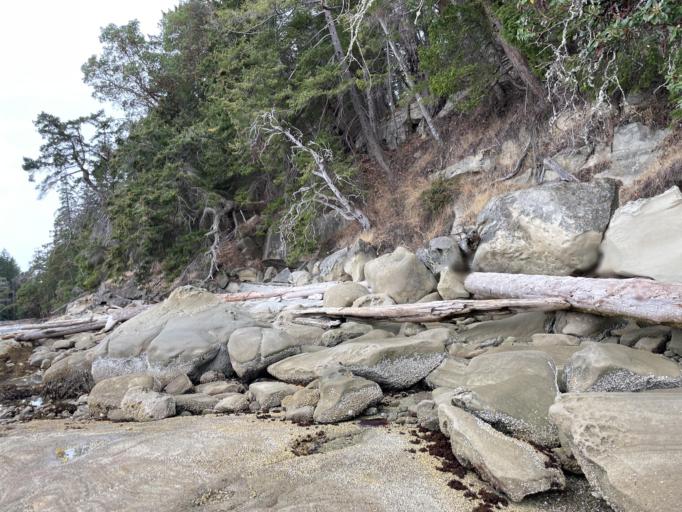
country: CA
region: British Columbia
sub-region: Cowichan Valley Regional District
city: Ladysmith
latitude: 49.0932
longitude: -123.7232
